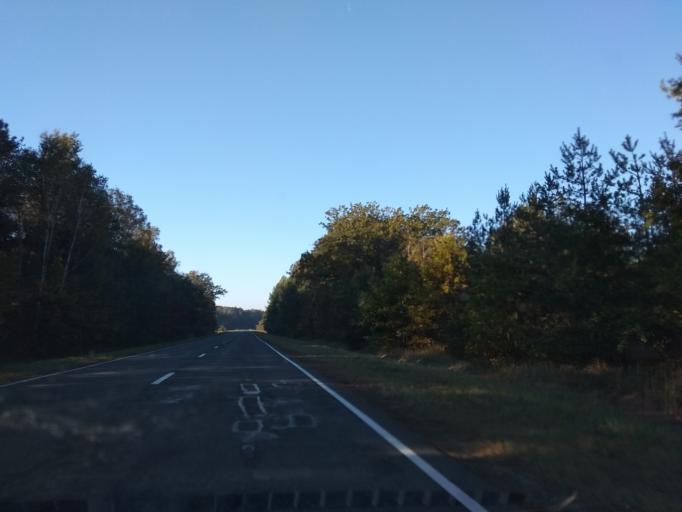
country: BY
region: Brest
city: Kobryn
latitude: 52.0169
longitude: 24.2372
